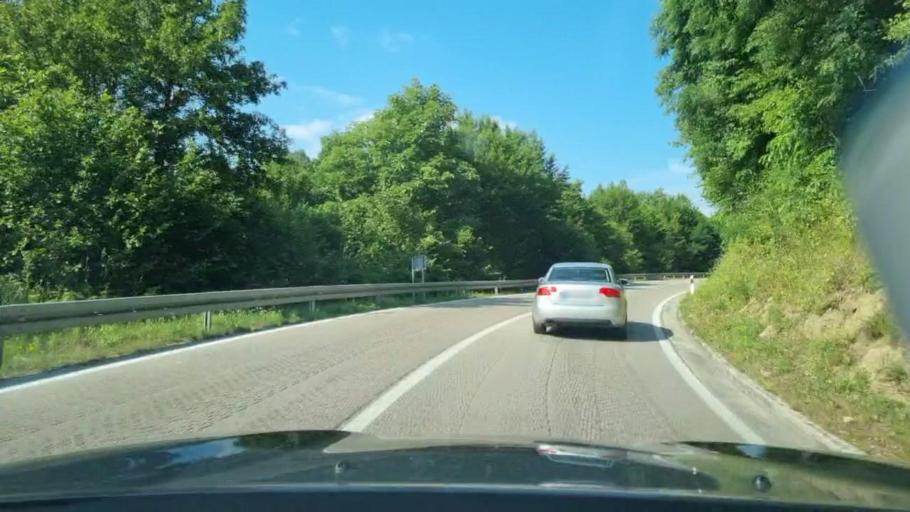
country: BA
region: Federation of Bosnia and Herzegovina
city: Skokovi
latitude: 45.0249
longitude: 15.9045
